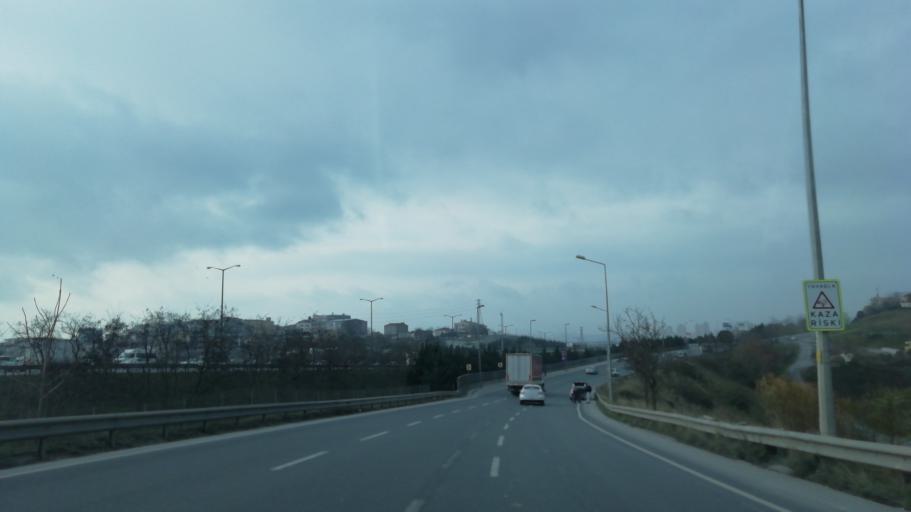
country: TR
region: Istanbul
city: Basaksehir
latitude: 41.0618
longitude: 28.7585
